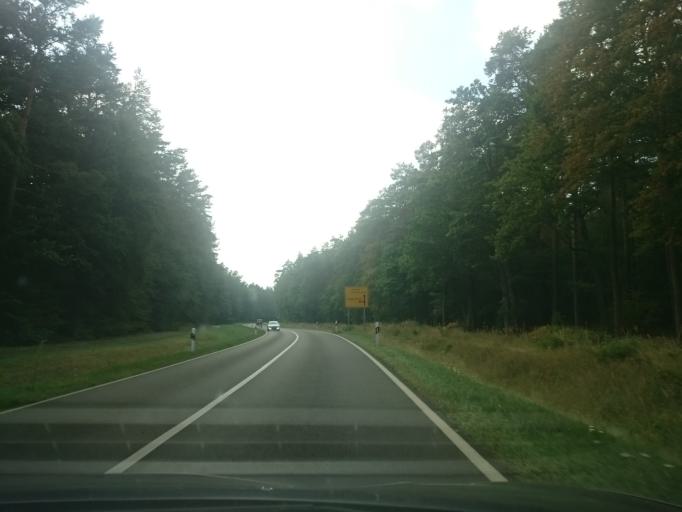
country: DE
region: Mecklenburg-Vorpommern
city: Torgelow
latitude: 53.6372
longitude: 13.9577
